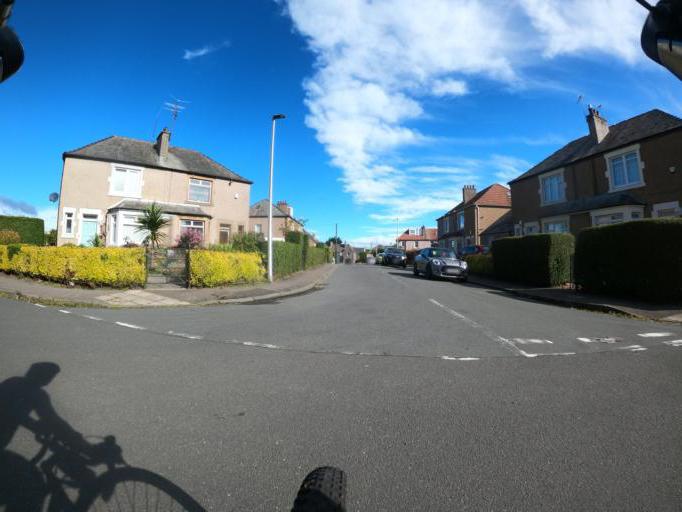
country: GB
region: Scotland
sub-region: Edinburgh
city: Edinburgh
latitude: 55.9669
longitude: -3.2430
